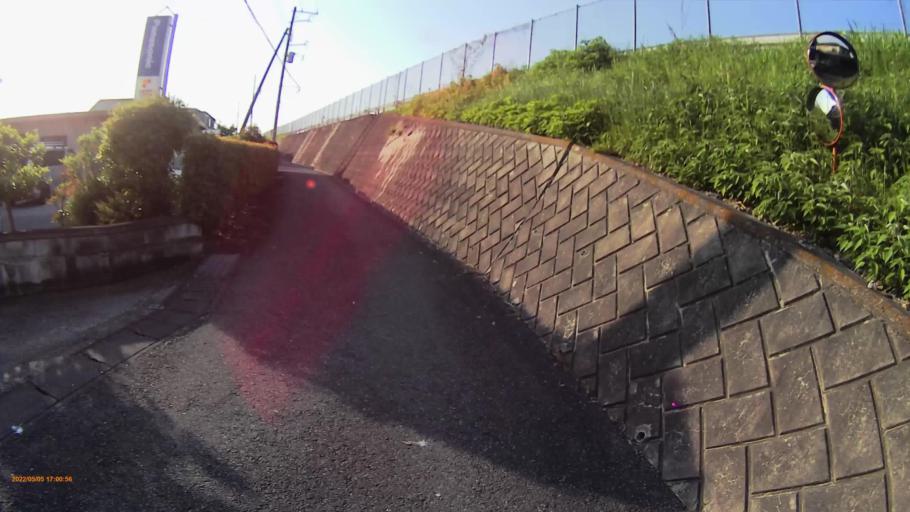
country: JP
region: Saitama
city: Kurihashi
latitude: 36.1155
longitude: 139.7223
